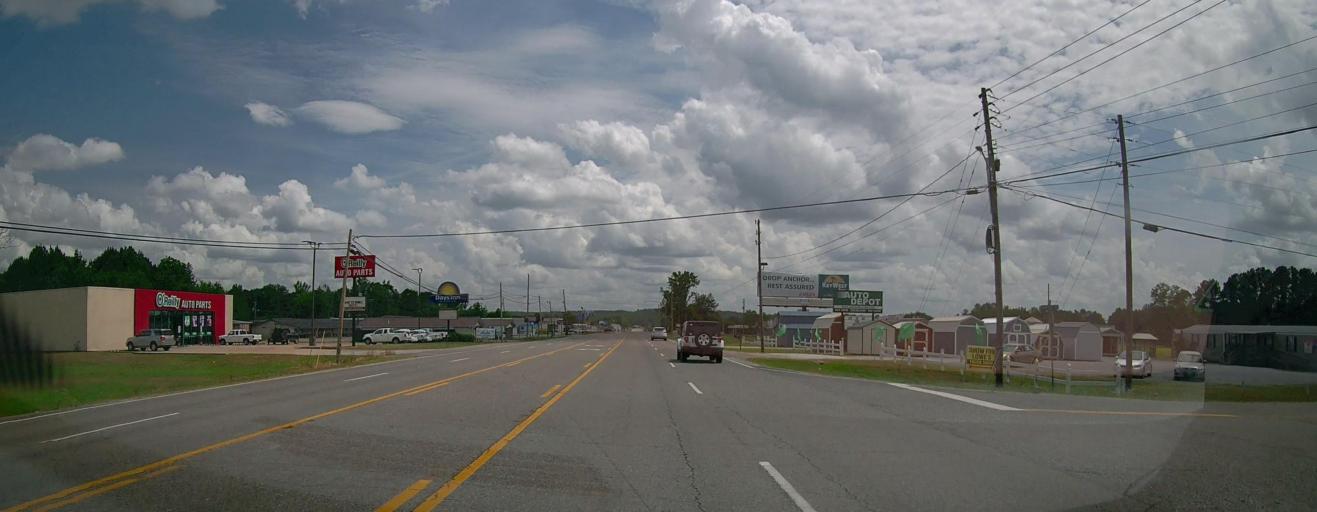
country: US
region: Alabama
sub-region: Marion County
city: Hamilton
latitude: 34.1178
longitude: -87.9896
